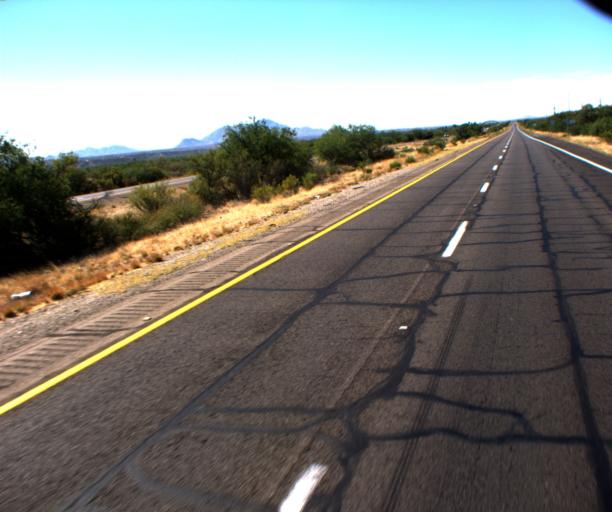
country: US
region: Arizona
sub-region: Pima County
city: Arivaca Junction
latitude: 31.6704
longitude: -111.0633
